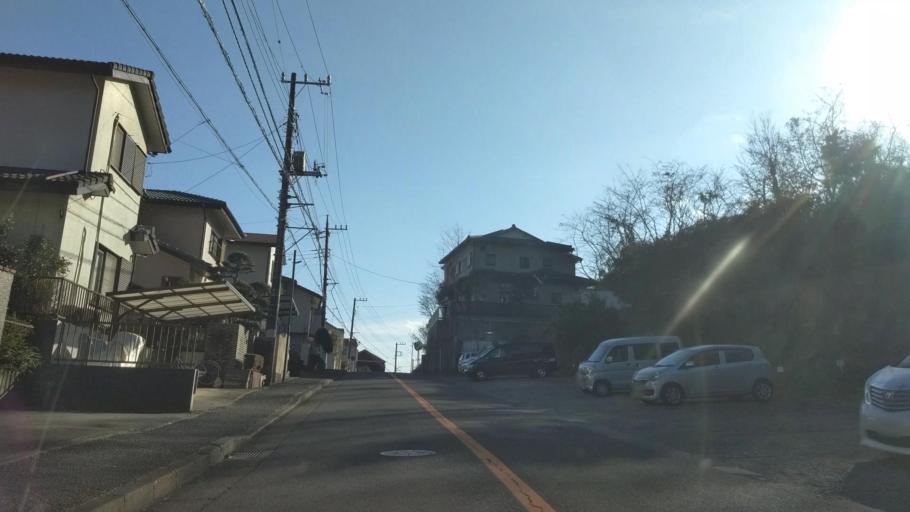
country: JP
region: Kanagawa
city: Hadano
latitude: 35.3668
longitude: 139.2515
